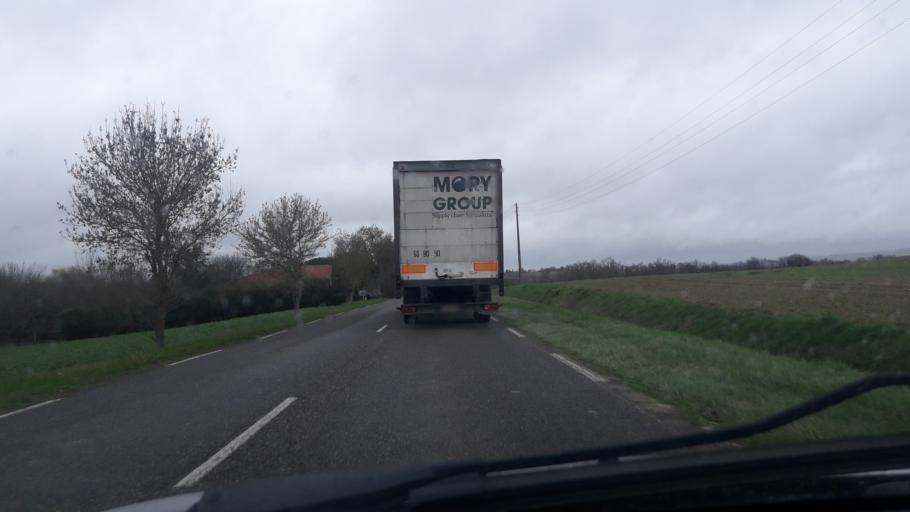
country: FR
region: Midi-Pyrenees
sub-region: Departement du Gers
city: Gimont
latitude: 43.7062
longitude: 0.9922
